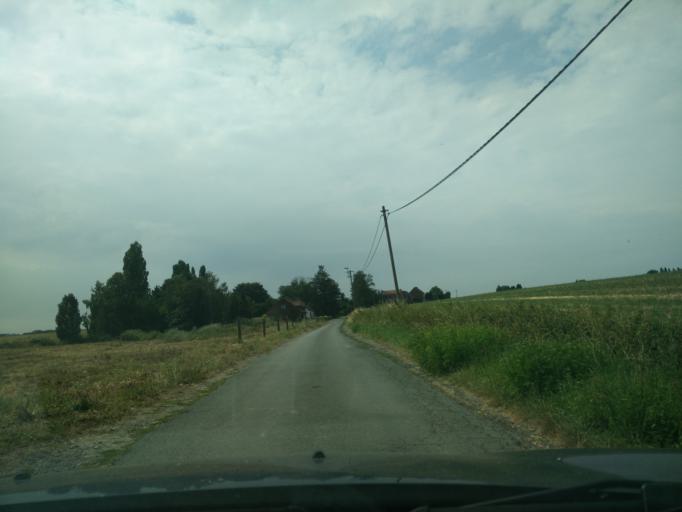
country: BE
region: Wallonia
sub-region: Province du Hainaut
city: Braine-le-Comte
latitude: 50.6294
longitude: 4.1631
